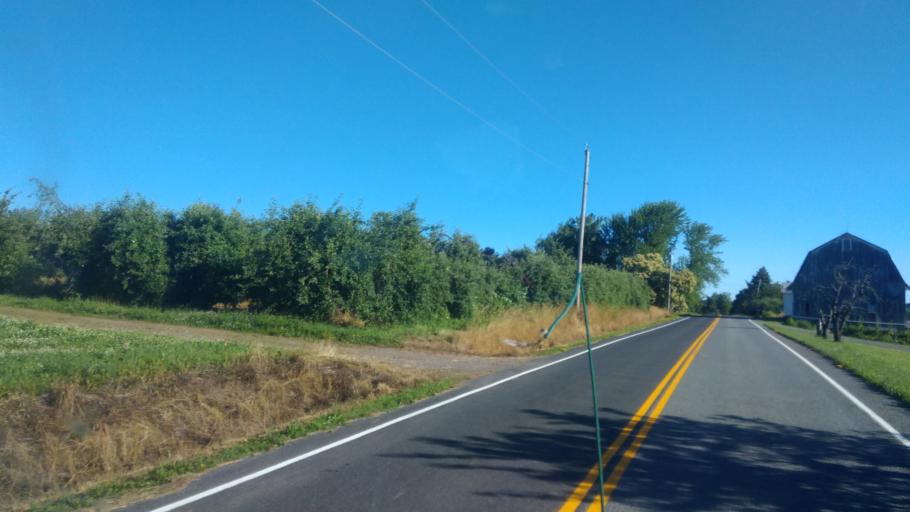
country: US
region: New York
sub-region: Wayne County
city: Sodus
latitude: 43.2048
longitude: -77.1033
